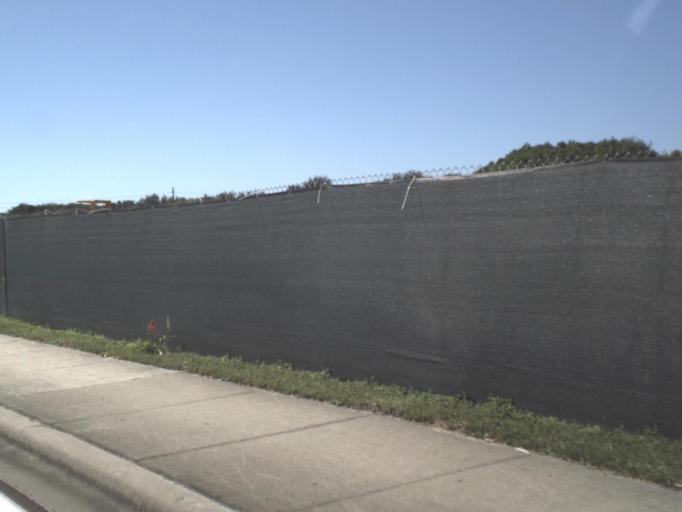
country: US
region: Florida
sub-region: Collier County
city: Naples
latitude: 26.1783
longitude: -81.7674
